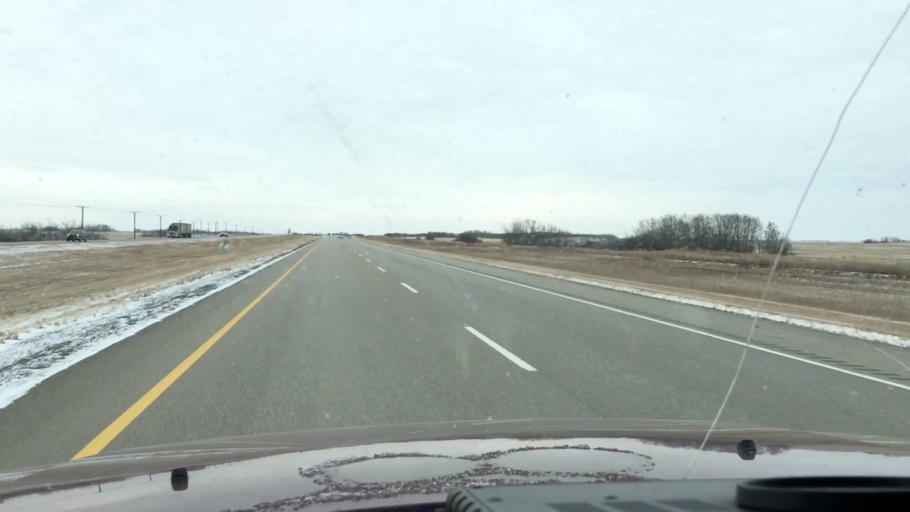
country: CA
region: Saskatchewan
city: Watrous
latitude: 51.3972
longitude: -106.1737
